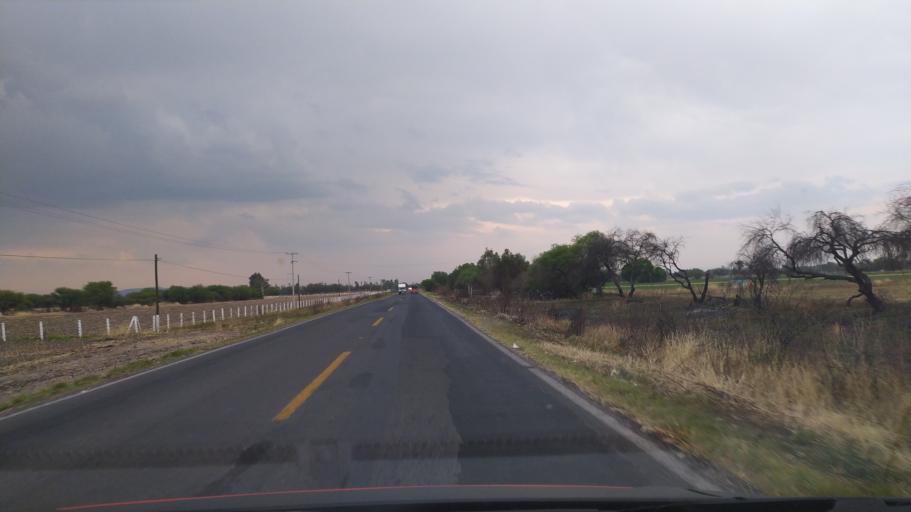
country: MX
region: Guanajuato
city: Ciudad Manuel Doblado
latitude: 20.7767
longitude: -101.9110
